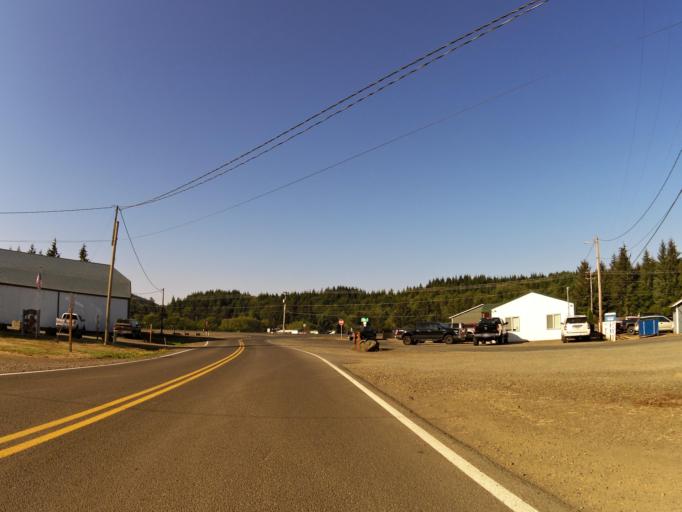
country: US
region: Oregon
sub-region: Tillamook County
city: Tillamook
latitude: 45.3836
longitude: -123.8030
